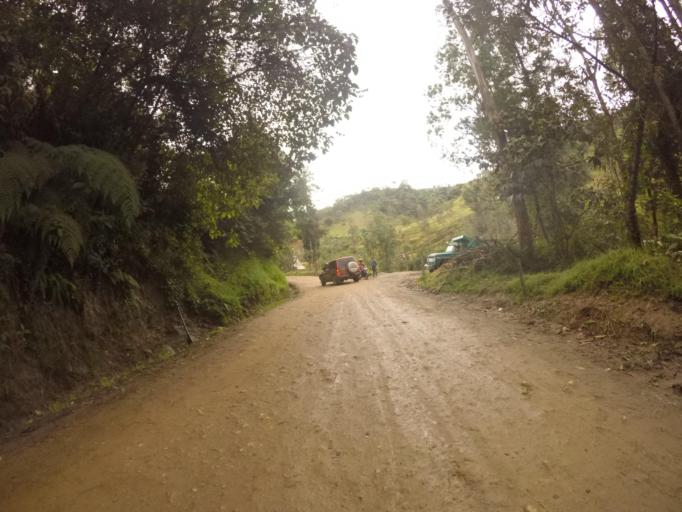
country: CO
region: Cauca
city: Silvia
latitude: 2.6253
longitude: -76.3723
